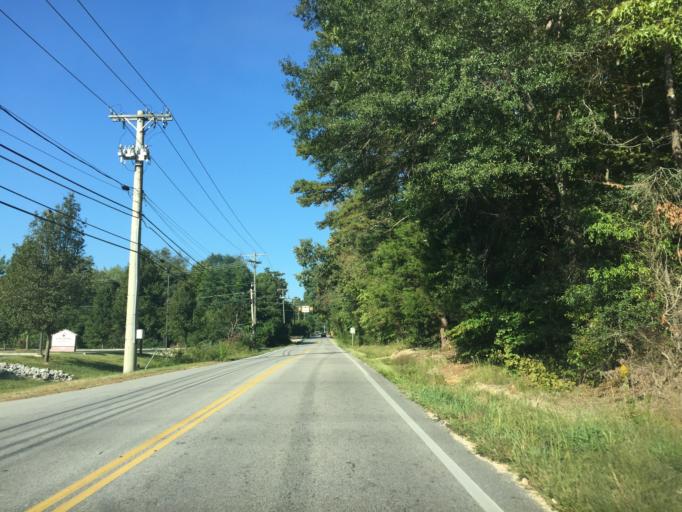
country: US
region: Tennessee
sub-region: Hamilton County
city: Harrison
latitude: 35.1216
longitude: -85.0941
